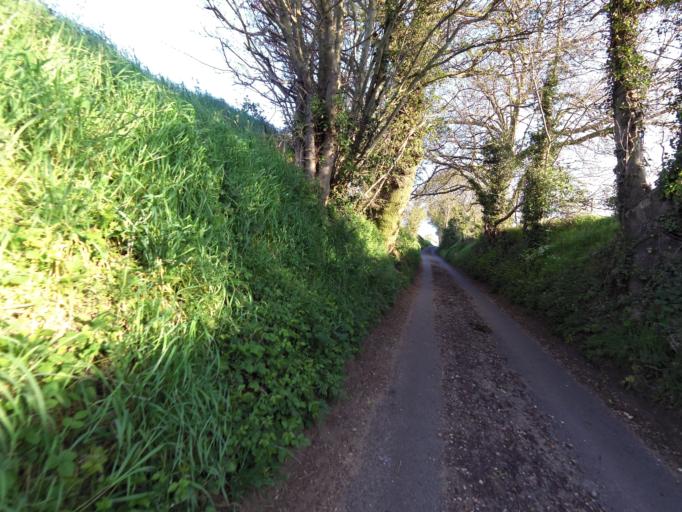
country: GB
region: England
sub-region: Suffolk
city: Bramford
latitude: 52.0427
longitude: 1.0718
